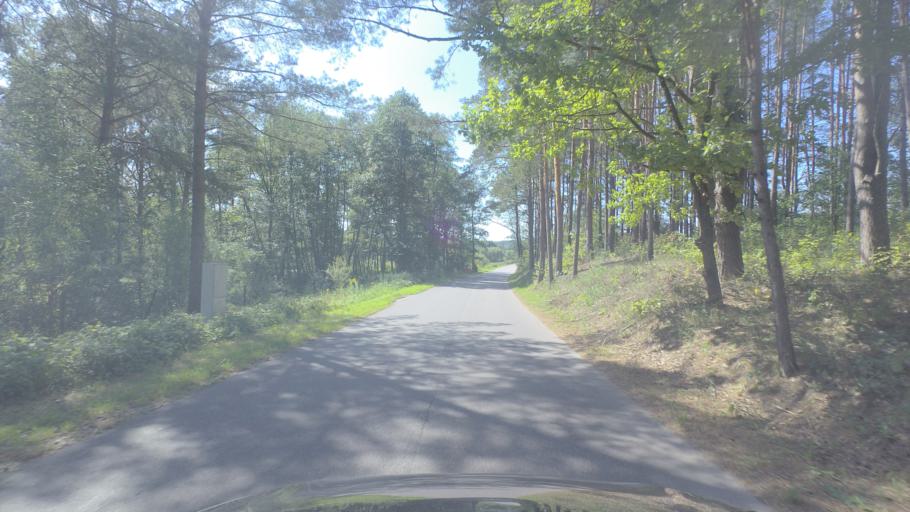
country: LT
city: Nemencine
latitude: 54.8619
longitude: 25.3967
